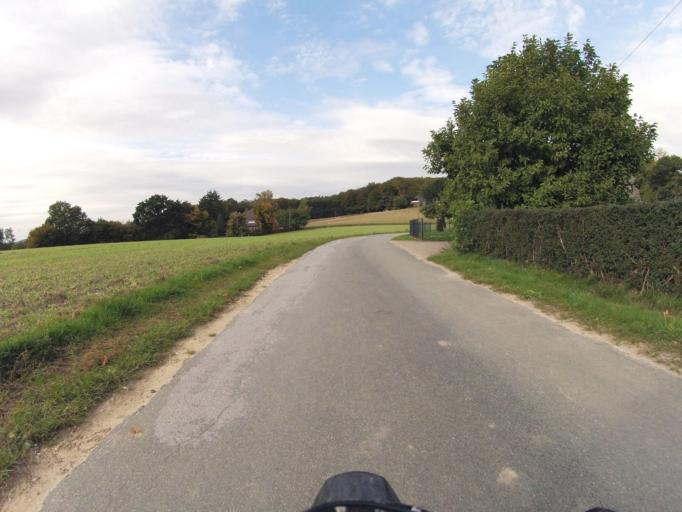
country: DE
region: North Rhine-Westphalia
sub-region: Regierungsbezirk Munster
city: Tecklenburg
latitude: 52.2691
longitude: 7.8062
